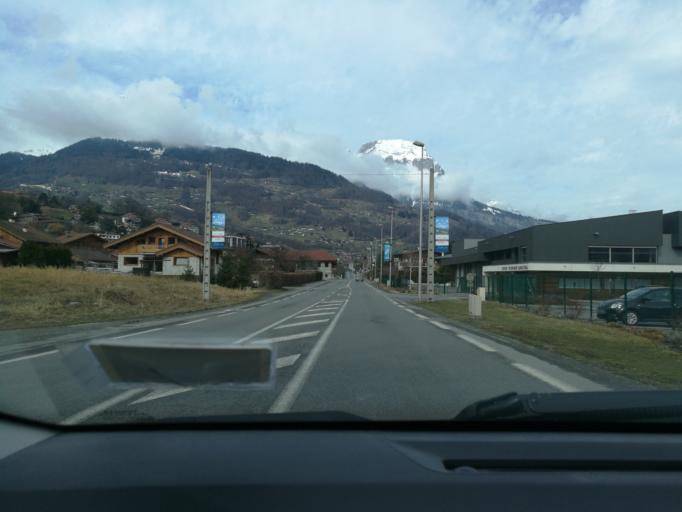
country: FR
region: Rhone-Alpes
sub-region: Departement de la Haute-Savoie
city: Domancy
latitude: 45.9278
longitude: 6.6389
